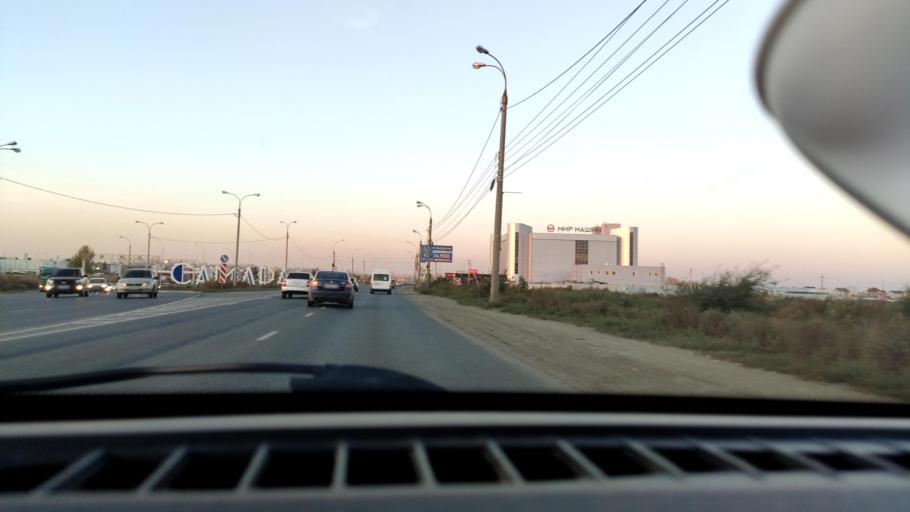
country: RU
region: Samara
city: Samara
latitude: 53.1328
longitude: 50.1733
